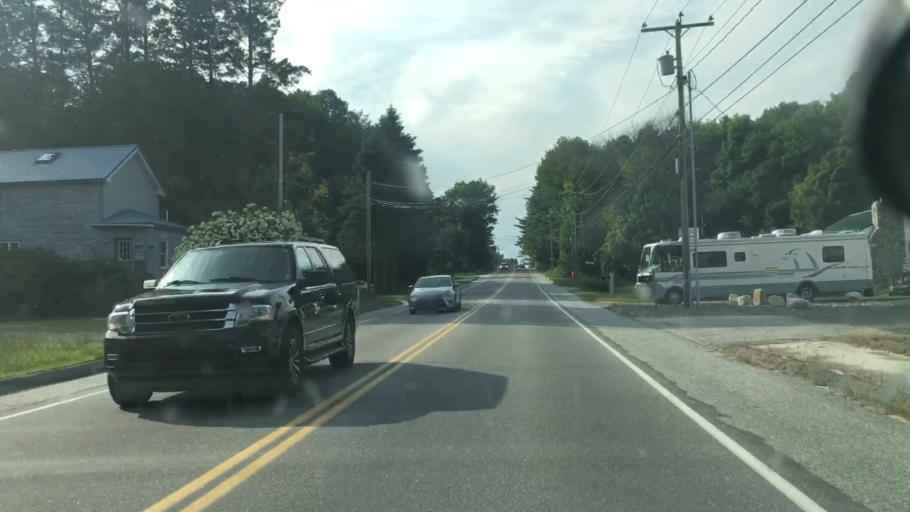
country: US
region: Maine
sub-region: Cumberland County
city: North Windham
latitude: 43.8131
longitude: -70.4236
